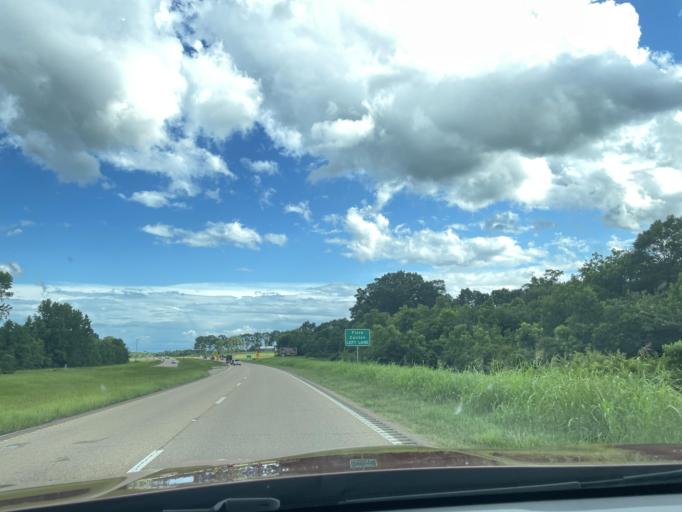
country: US
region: Mississippi
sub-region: Madison County
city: Flora
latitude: 32.5424
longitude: -90.3212
